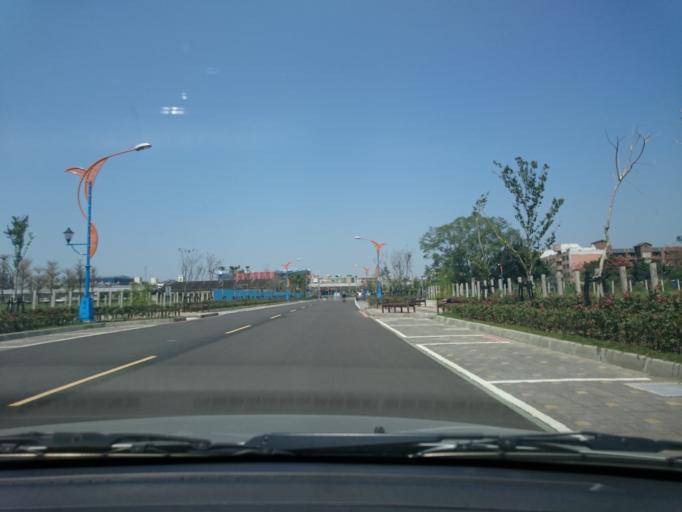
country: TW
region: Taiwan
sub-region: Taichung City
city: Taichung
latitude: 24.1357
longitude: 120.6930
